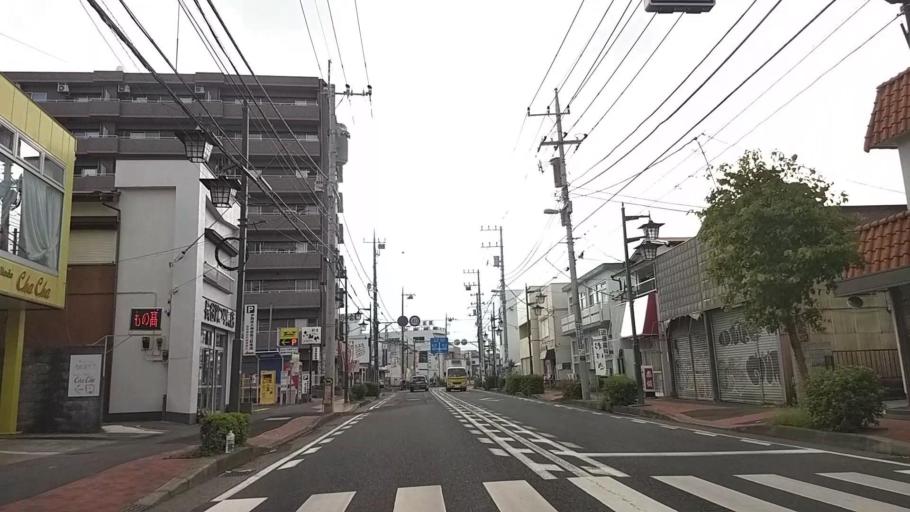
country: JP
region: Kanagawa
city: Isehara
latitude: 35.3984
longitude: 139.3066
